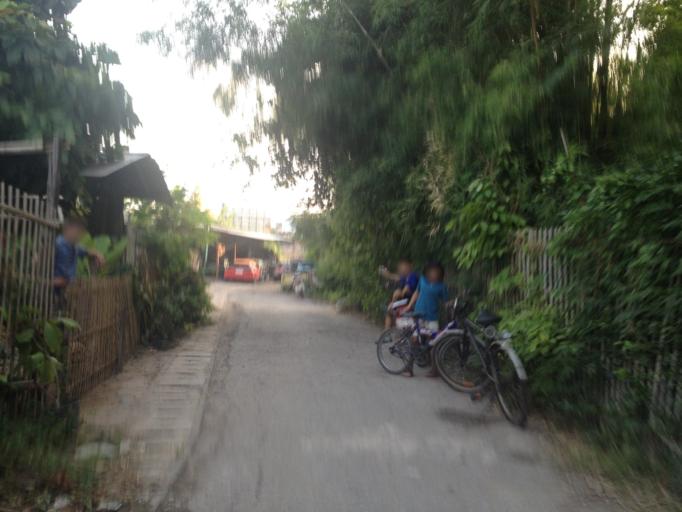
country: TH
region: Chiang Mai
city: Chiang Mai
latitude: 18.7612
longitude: 98.9434
